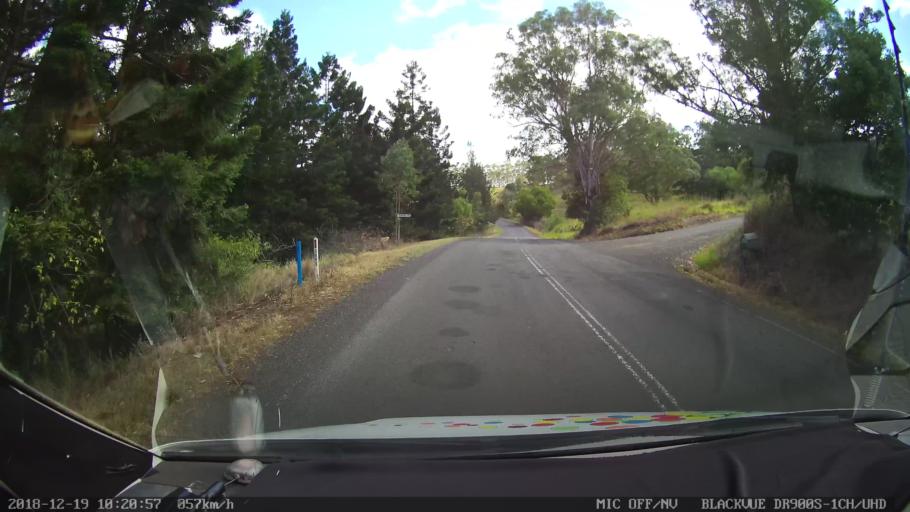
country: AU
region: New South Wales
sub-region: Kyogle
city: Kyogle
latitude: -28.6017
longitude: 153.0575
